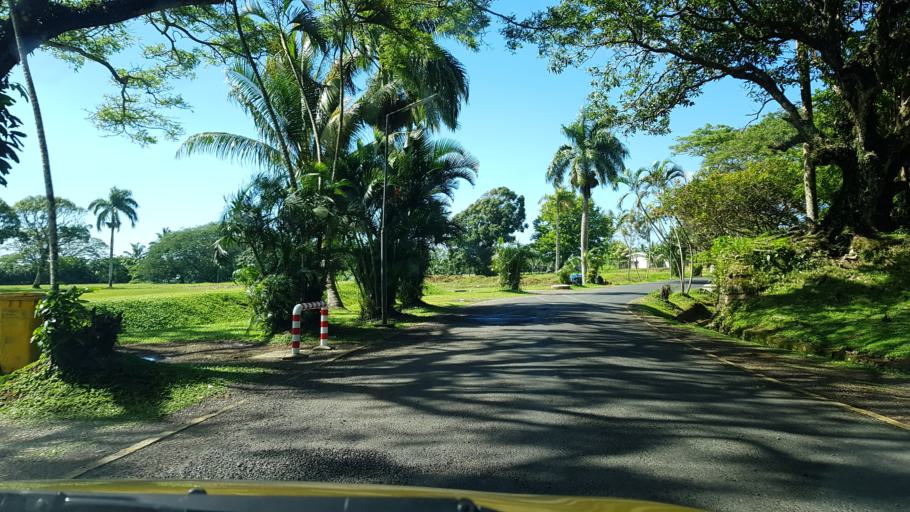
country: FJ
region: Central
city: Suva
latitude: -18.1547
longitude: 178.4441
